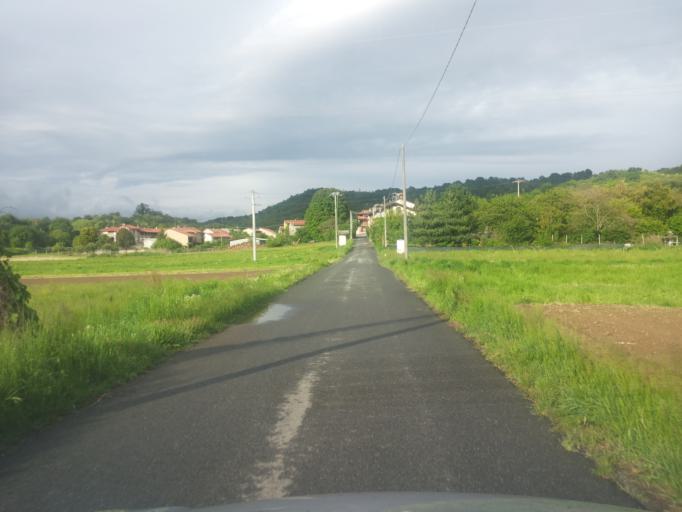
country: IT
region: Piedmont
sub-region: Provincia di Torino
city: Cossano Canavese
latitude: 45.3887
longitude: 8.0045
